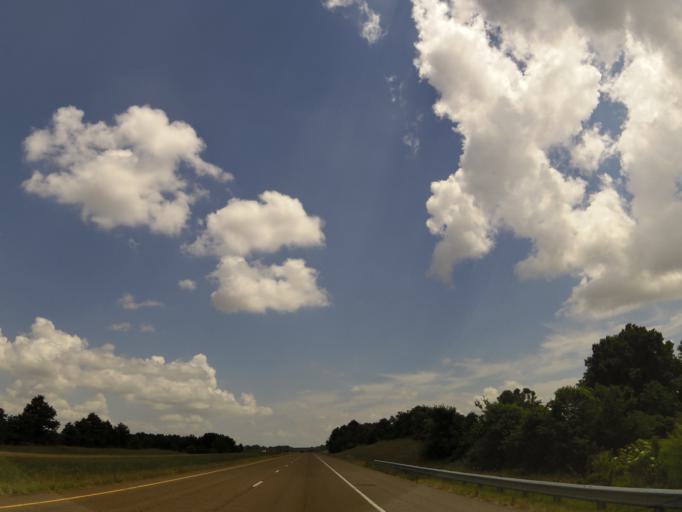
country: US
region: Tennessee
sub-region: Dyer County
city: Dyersburg
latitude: 35.9711
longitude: -89.3361
